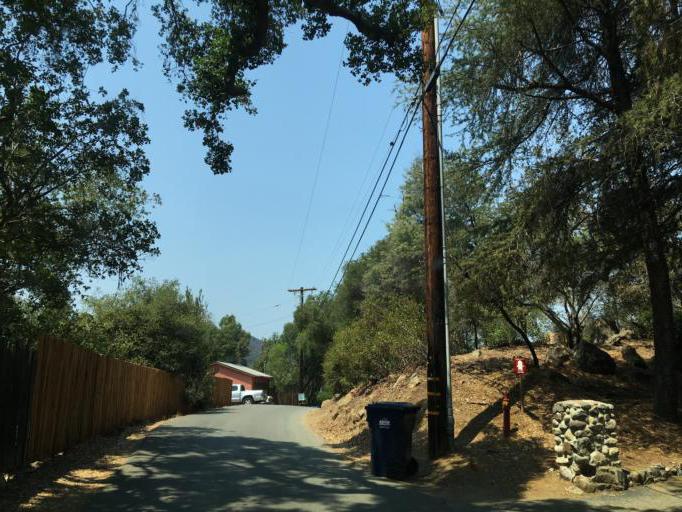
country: US
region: California
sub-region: Los Angeles County
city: Topanga
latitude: 34.1029
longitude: -118.5885
